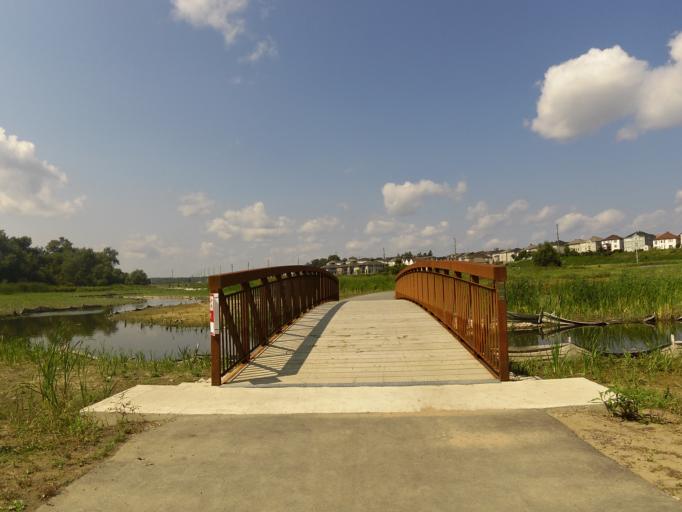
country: CA
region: Ontario
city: Bells Corners
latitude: 45.3098
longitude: -75.9333
